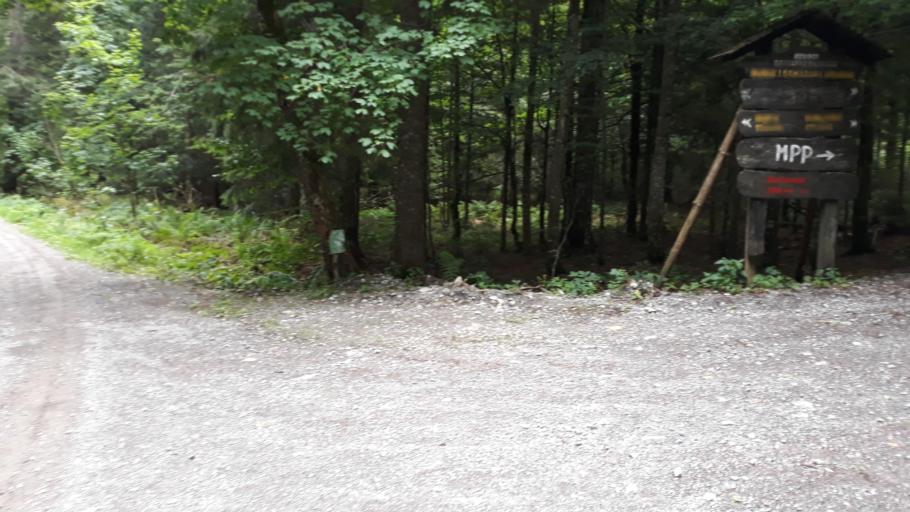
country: HR
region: Primorsko-Goranska
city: Vrbovsko
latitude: 45.2366
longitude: 14.9524
